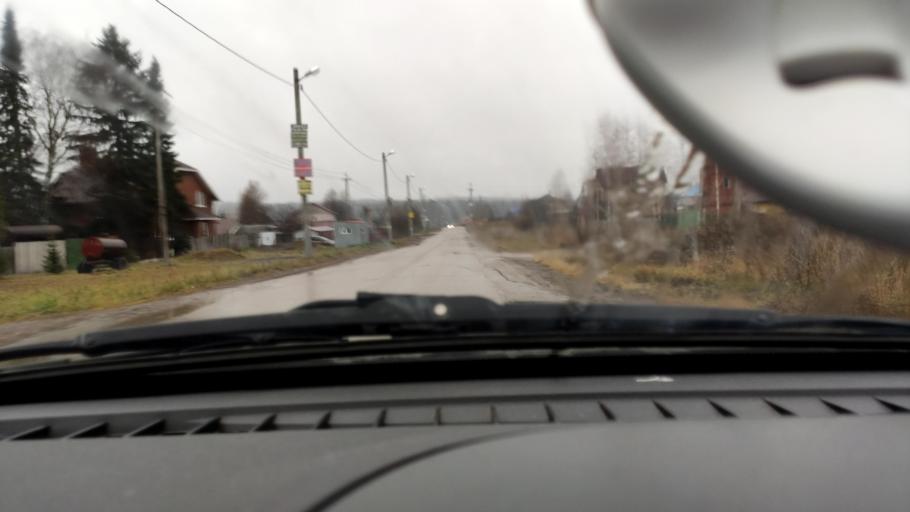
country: RU
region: Perm
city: Perm
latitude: 58.0412
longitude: 56.4081
